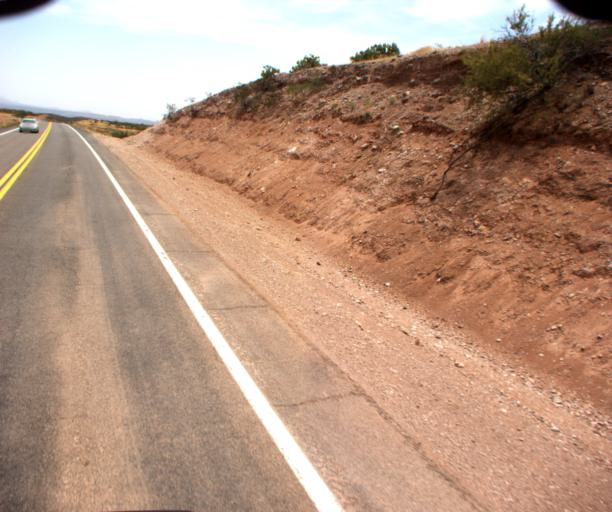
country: US
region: Arizona
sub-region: Graham County
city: Bylas
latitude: 33.2209
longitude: -110.2221
